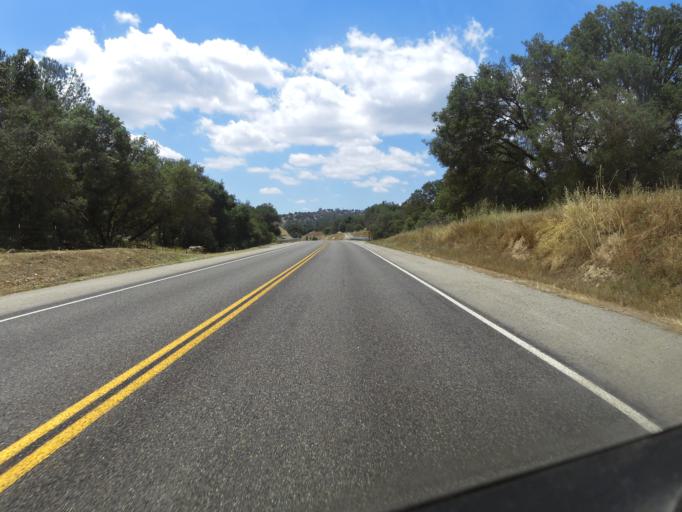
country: US
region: California
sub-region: Madera County
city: Coarsegold
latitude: 37.1525
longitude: -119.6588
